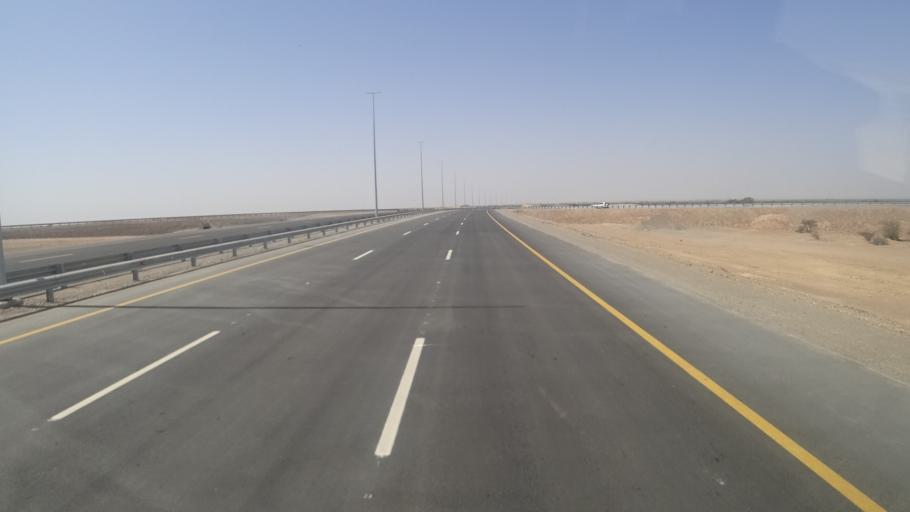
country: OM
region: Ash Sharqiyah
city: Sur
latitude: 22.2788
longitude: 59.2648
